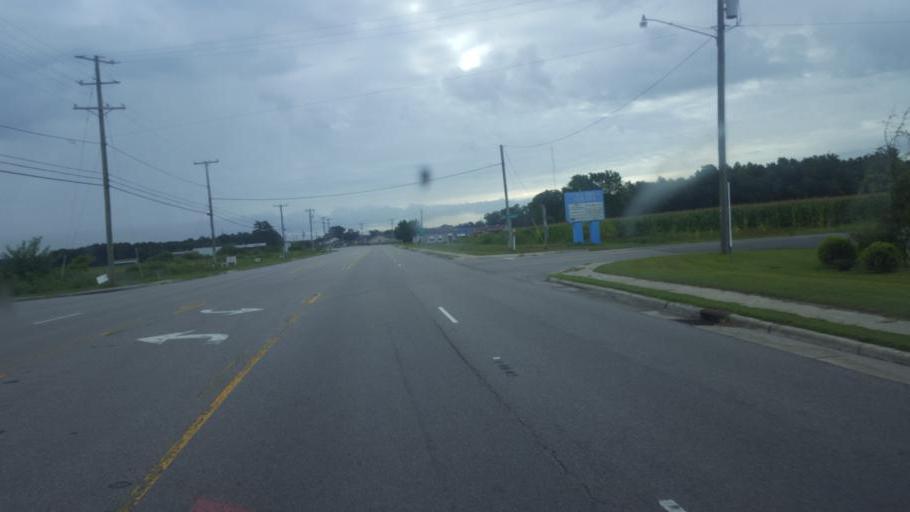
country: US
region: North Carolina
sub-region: Tyrrell County
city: Columbia
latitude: 35.9189
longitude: -76.2412
